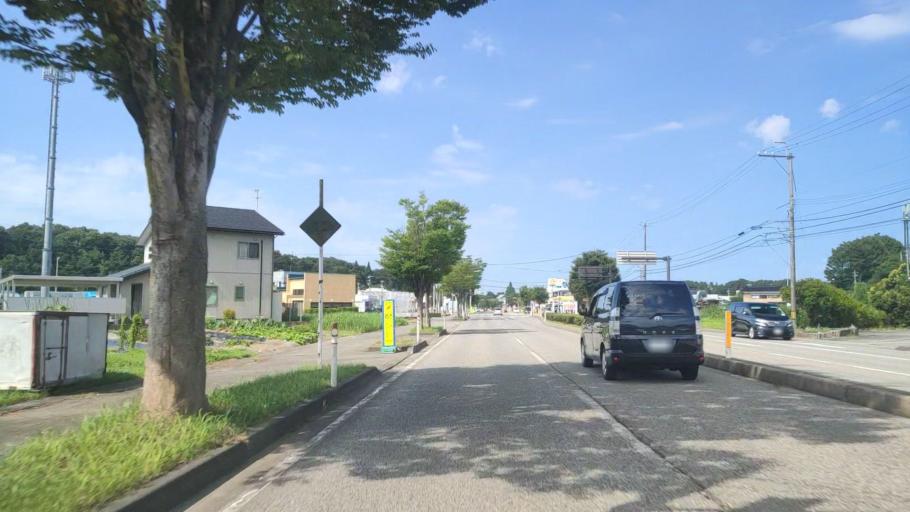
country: JP
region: Ishikawa
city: Matsuto
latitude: 36.4437
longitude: 136.5500
